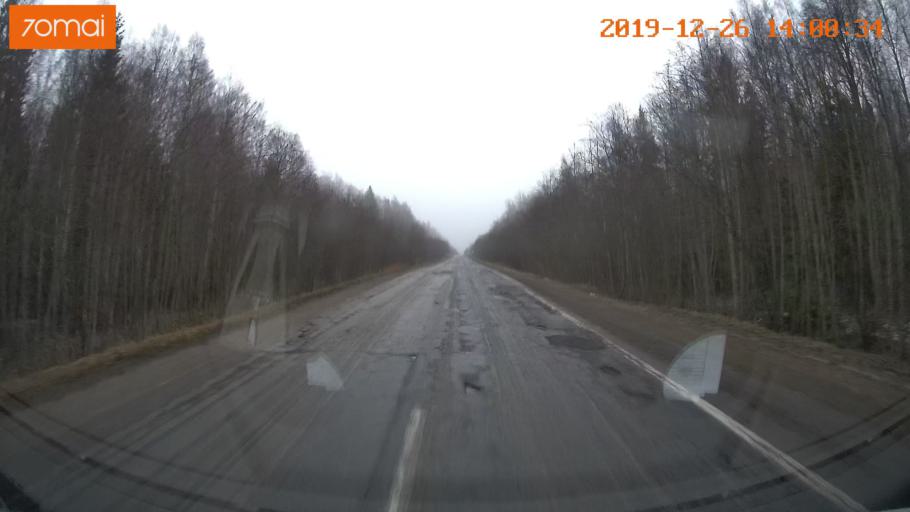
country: RU
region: Jaroslavl
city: Poshekhon'ye
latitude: 58.5572
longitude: 38.7459
